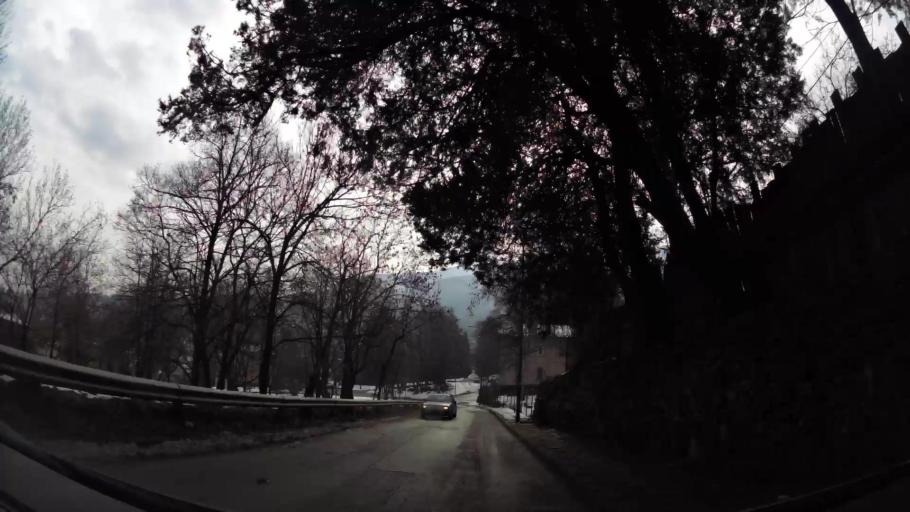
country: BG
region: Sofia-Capital
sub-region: Stolichna Obshtina
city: Sofia
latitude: 42.6463
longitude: 23.2674
